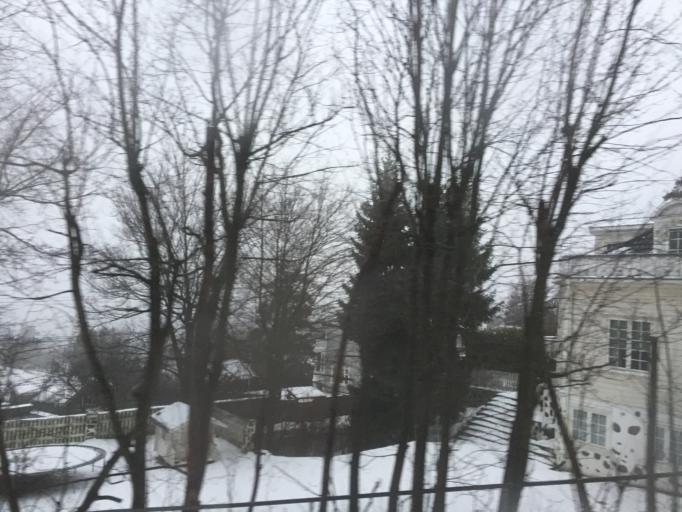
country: NO
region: Oslo
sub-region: Oslo
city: Sjolyststranda
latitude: 59.9584
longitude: 10.6702
